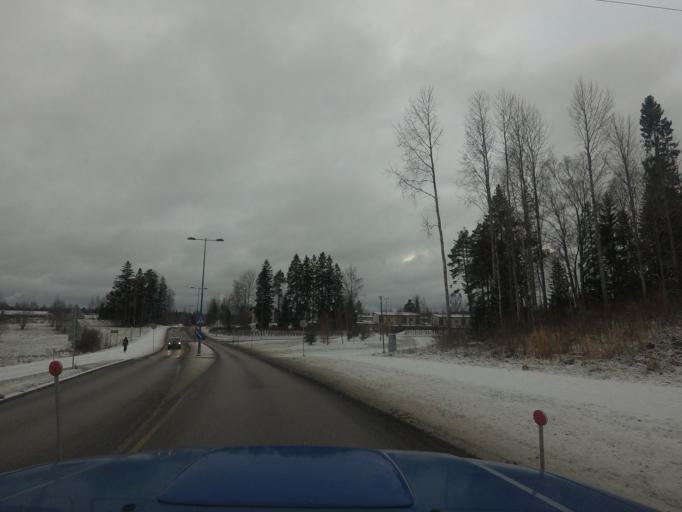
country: FI
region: Uusimaa
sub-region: Helsinki
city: Espoo
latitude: 60.1714
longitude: 24.6577
